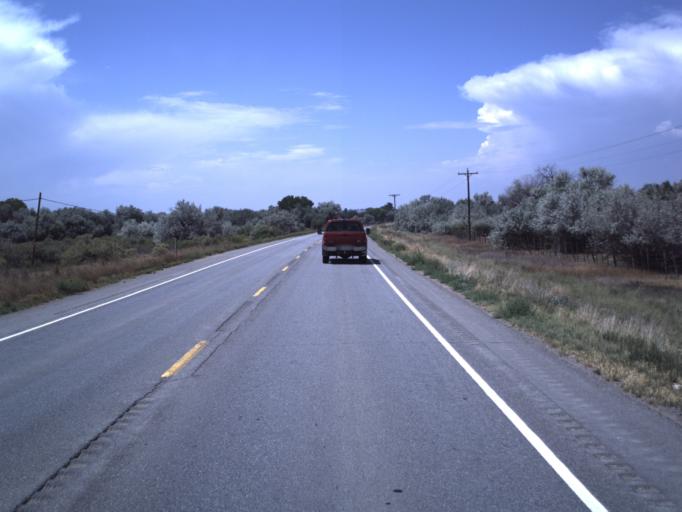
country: US
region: Utah
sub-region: Duchesne County
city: Roosevelt
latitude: 40.3021
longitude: -109.7990
